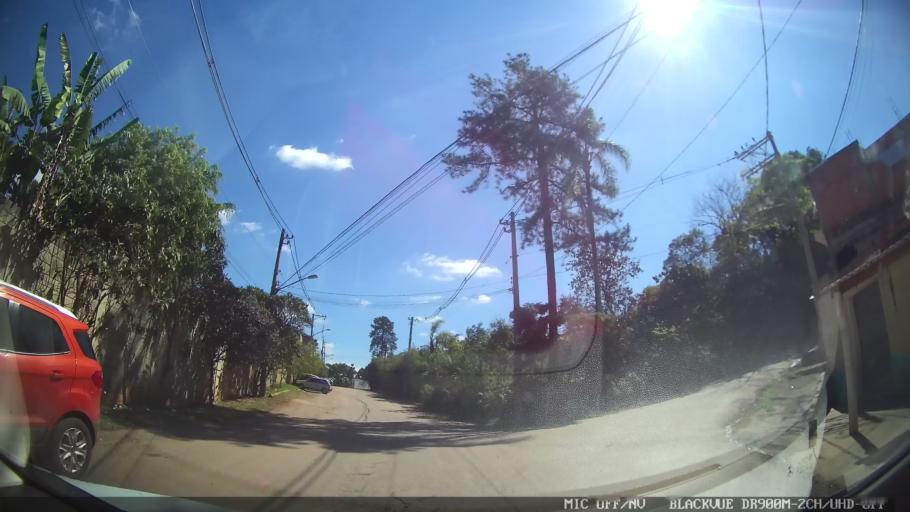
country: BR
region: Sao Paulo
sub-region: Cajamar
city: Cajamar
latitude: -23.4139
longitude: -46.8126
